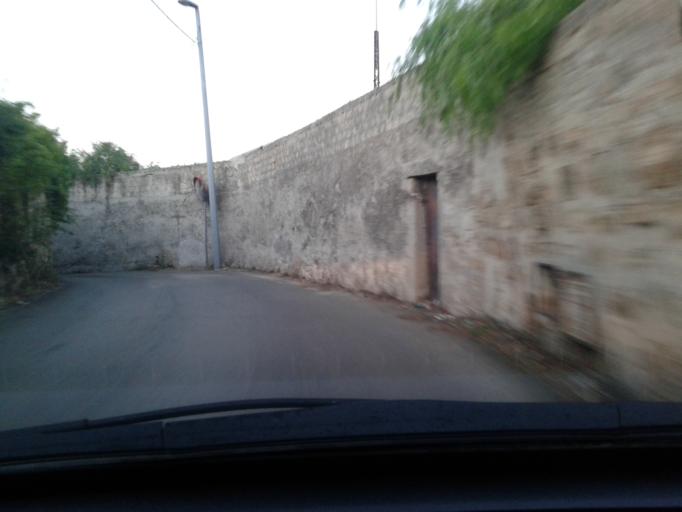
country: IT
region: Sicily
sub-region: Palermo
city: Palermo
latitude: 38.1055
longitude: 13.3279
